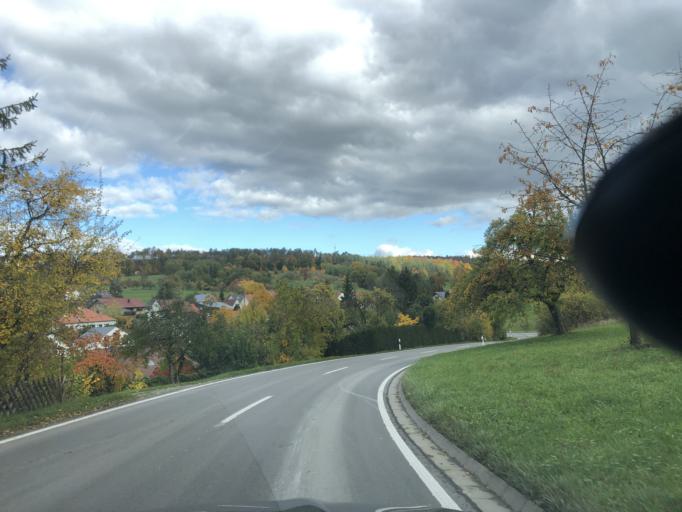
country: DE
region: Baden-Wuerttemberg
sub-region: Regierungsbezirk Stuttgart
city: Winterbach
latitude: 48.8281
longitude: 9.4641
